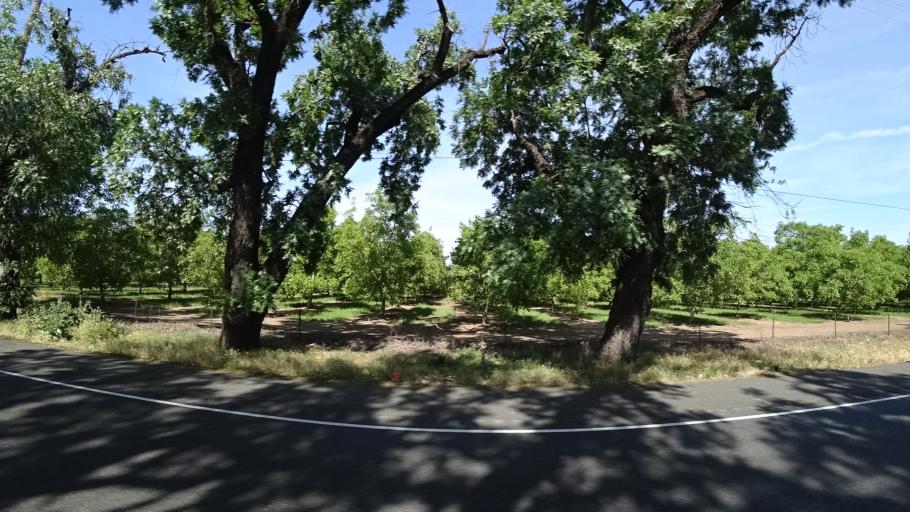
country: US
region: California
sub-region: Tehama County
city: Red Bluff
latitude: 40.1744
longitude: -122.1668
